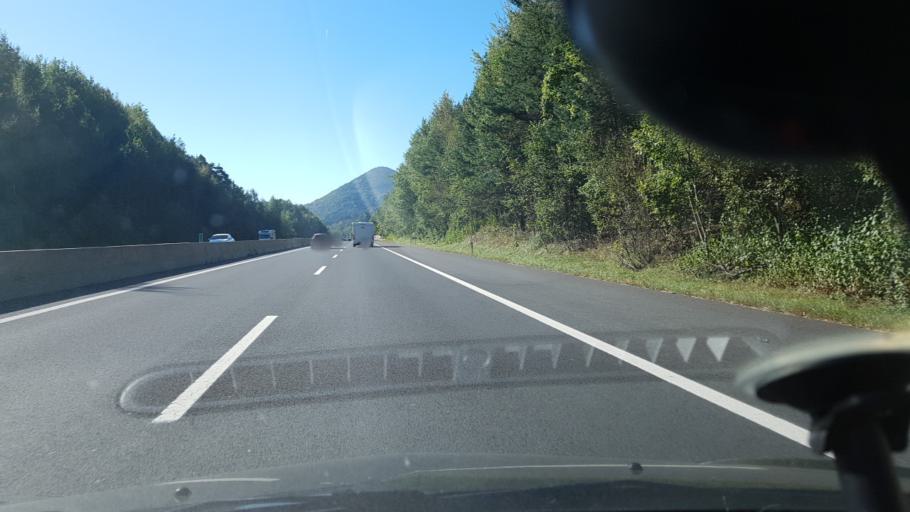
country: AT
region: Lower Austria
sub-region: Politischer Bezirk Neunkirchen
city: Warth
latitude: 47.6613
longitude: 16.1255
